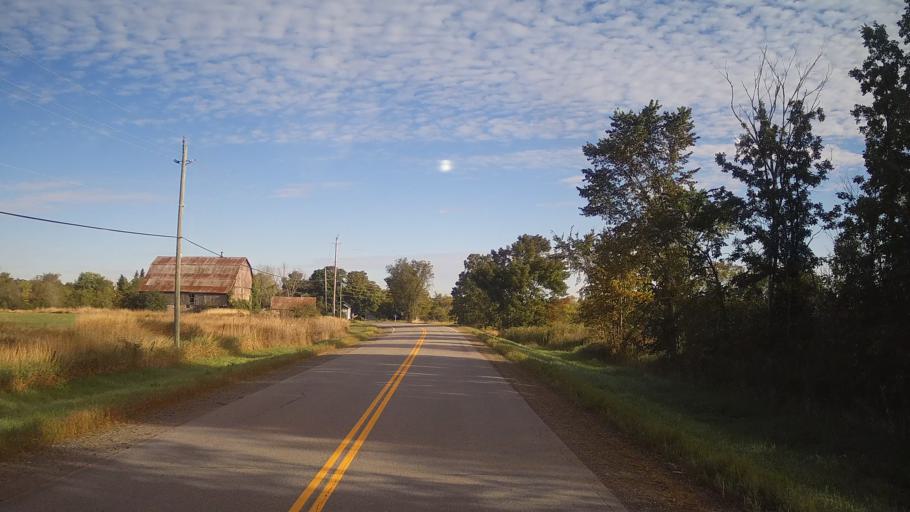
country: CA
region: Ontario
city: Gananoque
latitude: 44.3823
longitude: -76.1380
